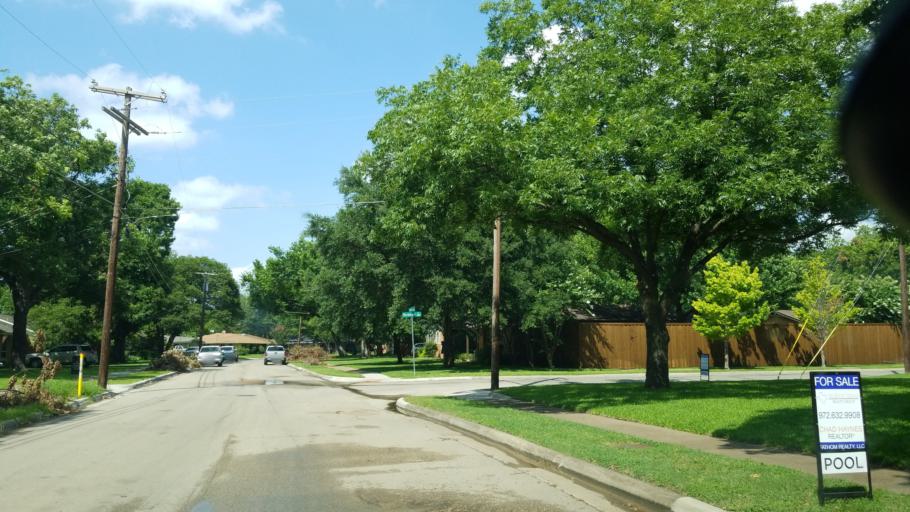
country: US
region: Texas
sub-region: Dallas County
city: Farmers Branch
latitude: 32.8854
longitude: -96.8586
